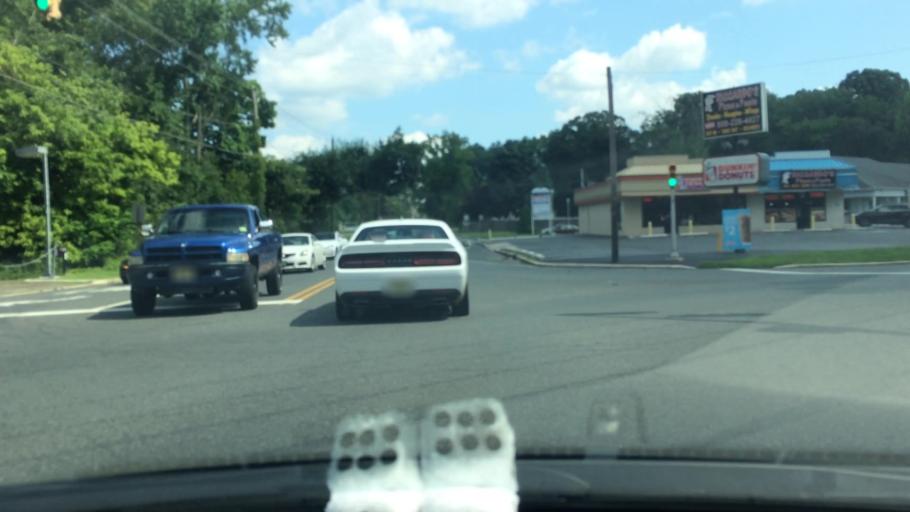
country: US
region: New Jersey
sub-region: Camden County
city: Blackwood
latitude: 39.8057
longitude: -75.0949
